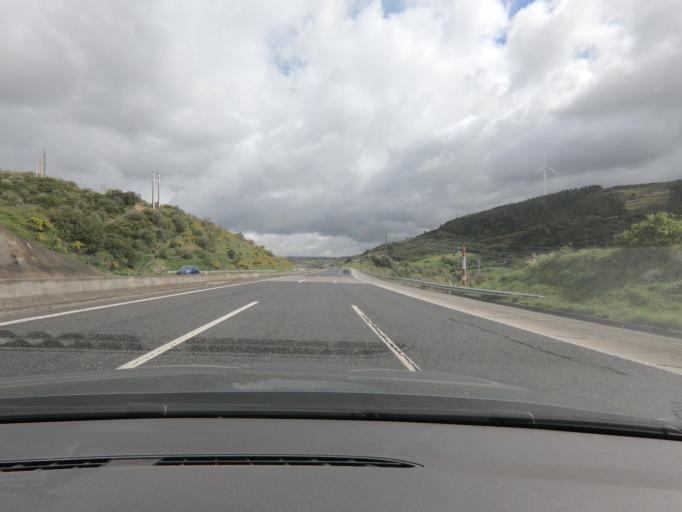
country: PT
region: Lisbon
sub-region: Loures
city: Bucelas
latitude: 38.8852
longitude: -9.1289
